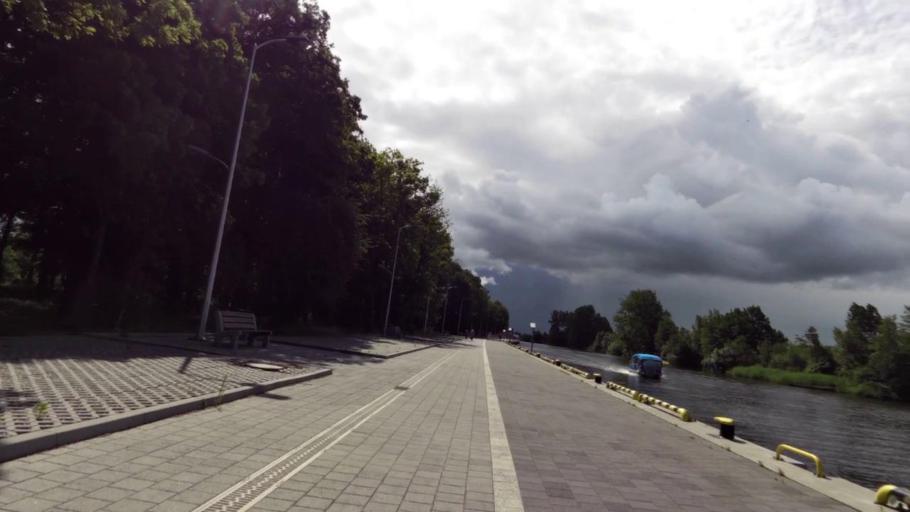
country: PL
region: West Pomeranian Voivodeship
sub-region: Powiat slawienski
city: Darlowo
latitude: 54.4326
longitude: 16.3911
